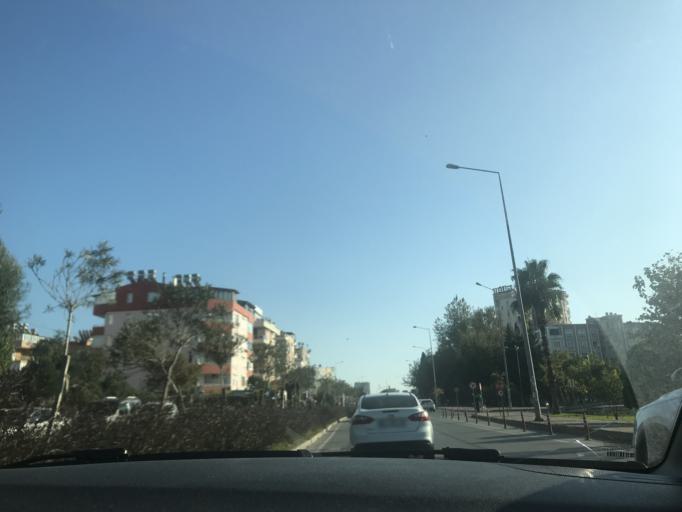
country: TR
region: Antalya
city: Antalya
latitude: 36.8815
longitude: 30.6494
